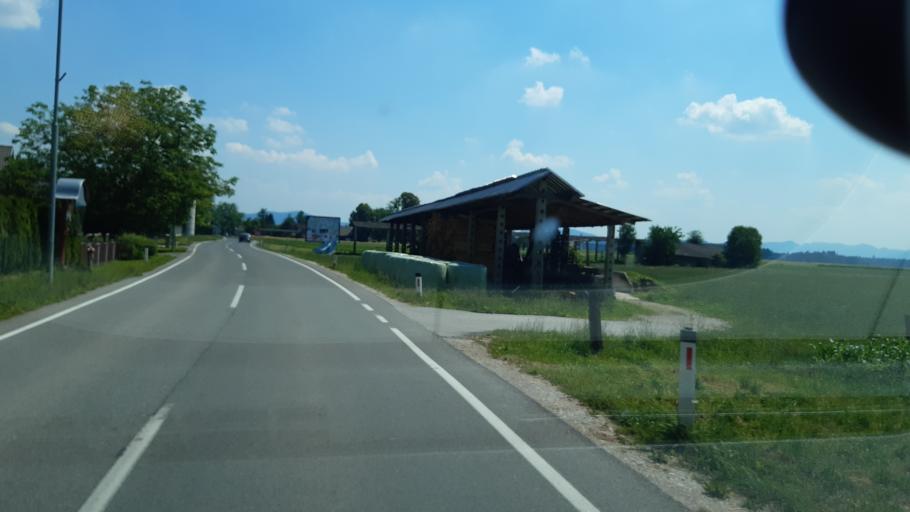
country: SI
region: Cerklje na Gorenjskem
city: Cerklje na Gorenjskem
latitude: 46.2378
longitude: 14.4847
